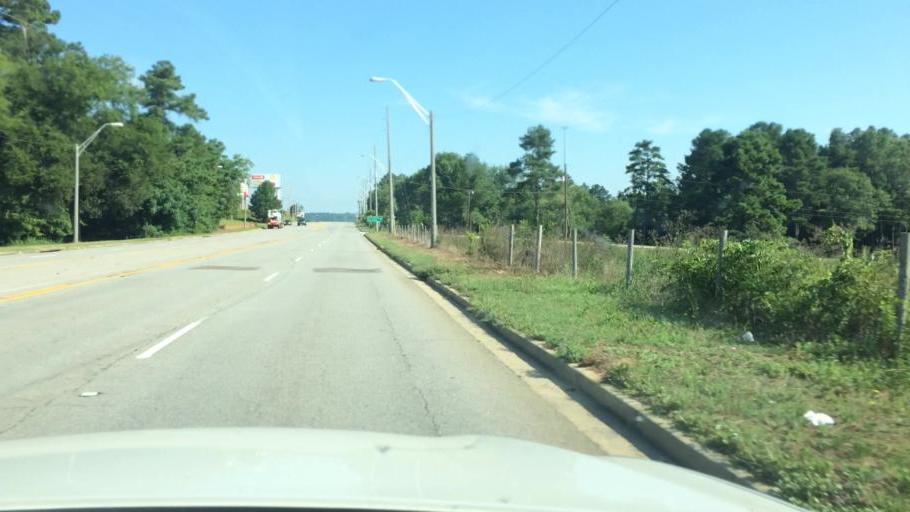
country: US
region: South Carolina
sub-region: Aiken County
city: North Augusta
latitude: 33.5332
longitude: -81.9864
